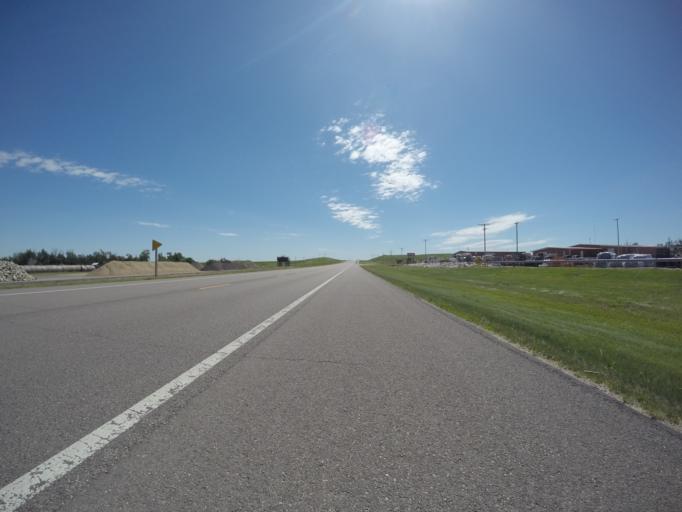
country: US
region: Kansas
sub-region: Rawlins County
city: Atwood
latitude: 39.8135
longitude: -101.0311
